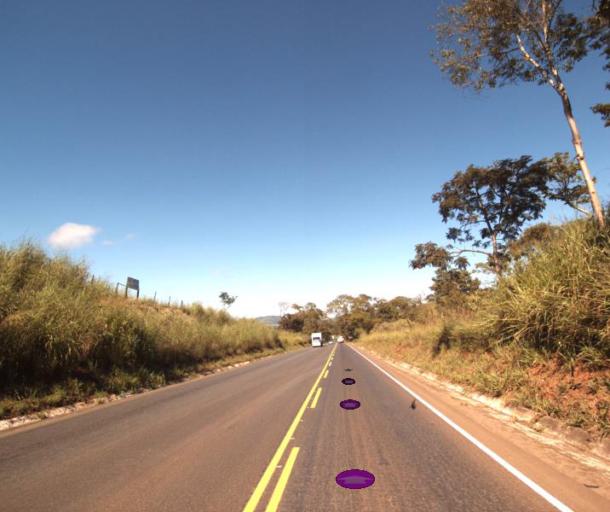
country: BR
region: Goias
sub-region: Ceres
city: Ceres
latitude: -15.1469
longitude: -49.5327
